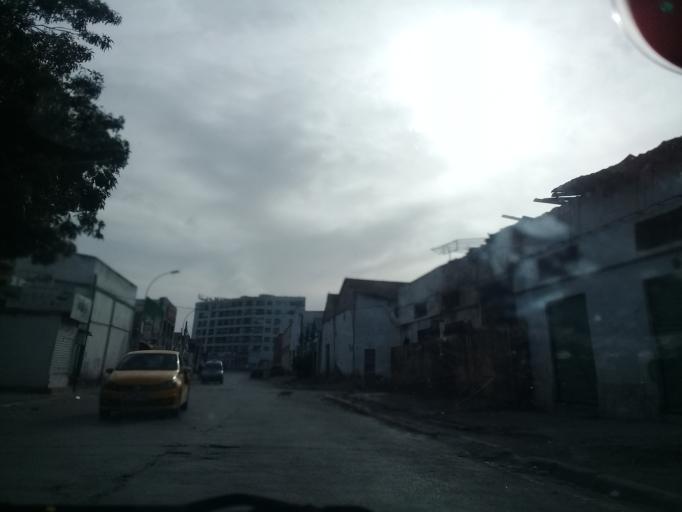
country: TN
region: Tunis
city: Tunis
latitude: 36.7912
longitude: 10.1863
